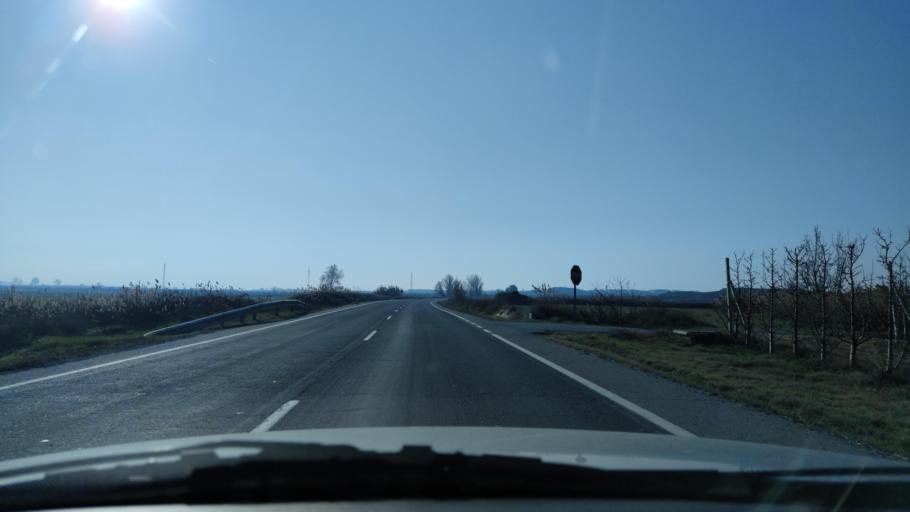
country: ES
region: Catalonia
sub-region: Provincia de Lleida
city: Albesa
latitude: 41.7151
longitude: 0.6394
